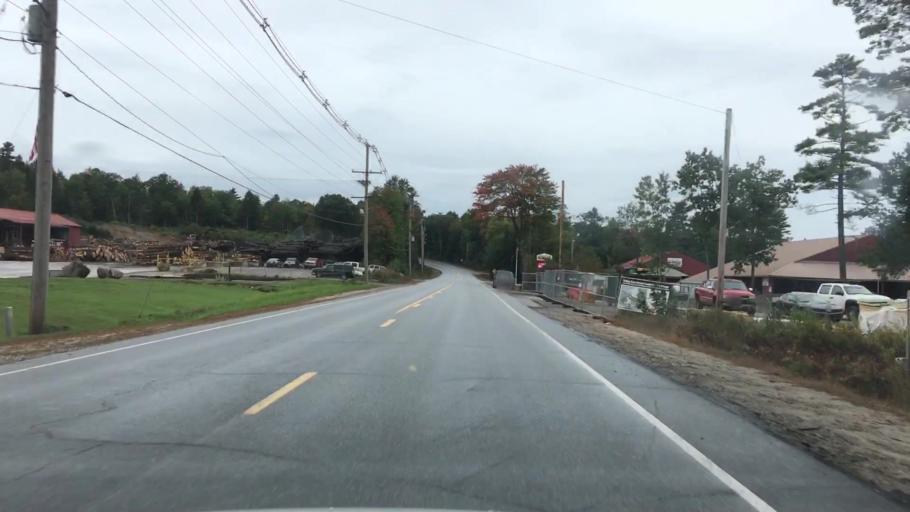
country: US
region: Maine
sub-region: Cumberland County
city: Raymond
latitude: 43.9851
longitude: -70.5461
